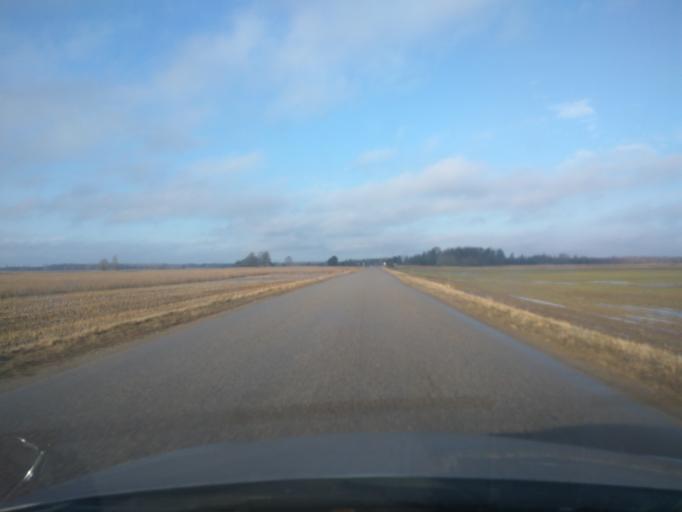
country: LV
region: Saldus Rajons
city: Saldus
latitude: 56.8194
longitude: 22.3781
